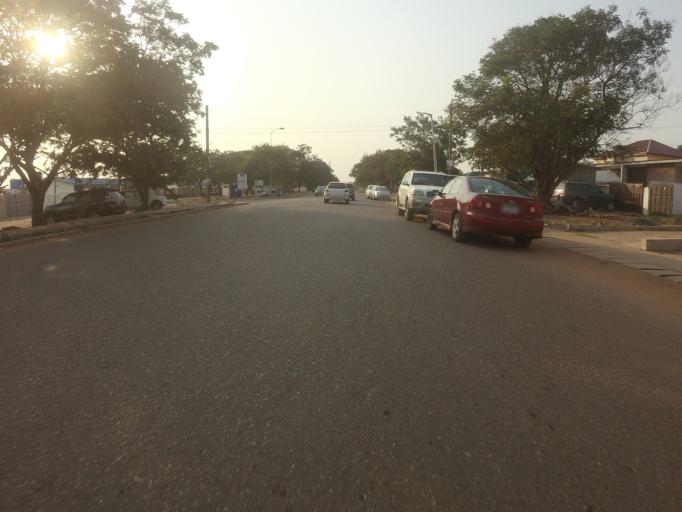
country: GH
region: Greater Accra
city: Nungua
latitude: 5.6228
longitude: -0.0588
